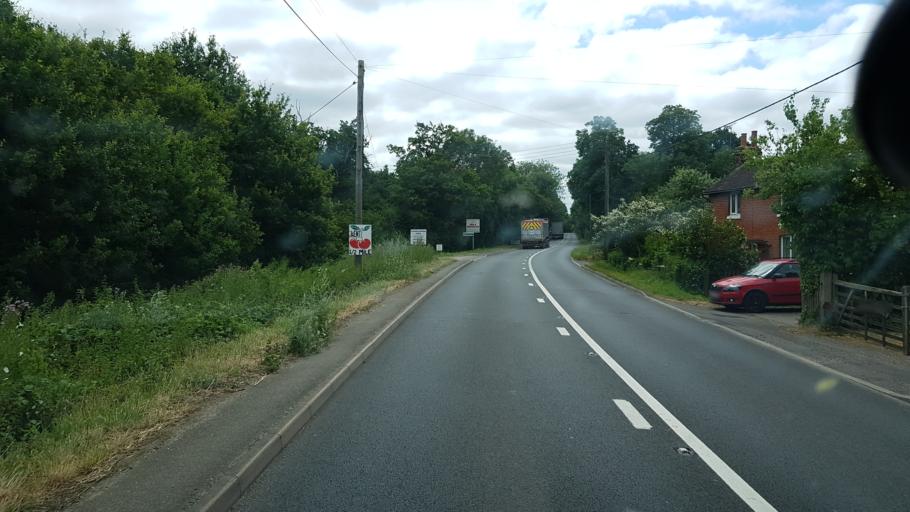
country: GB
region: England
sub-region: Surrey
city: Lingfield
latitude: 51.1848
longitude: -0.0469
